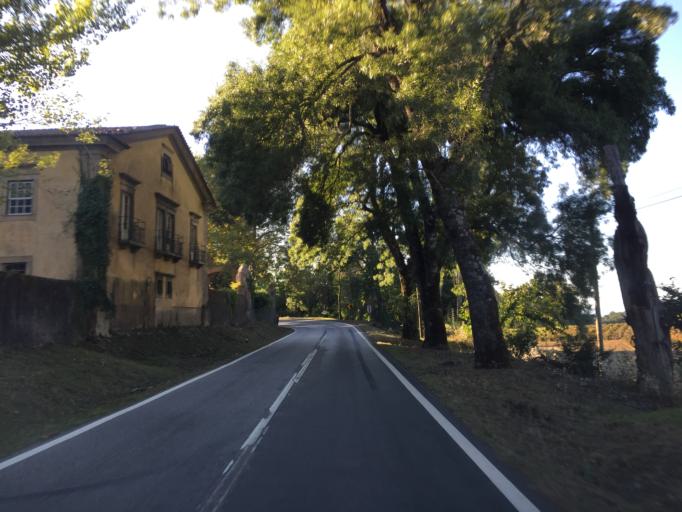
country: PT
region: Portalegre
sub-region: Castelo de Vide
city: Castelo de Vide
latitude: 39.4002
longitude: -7.4300
